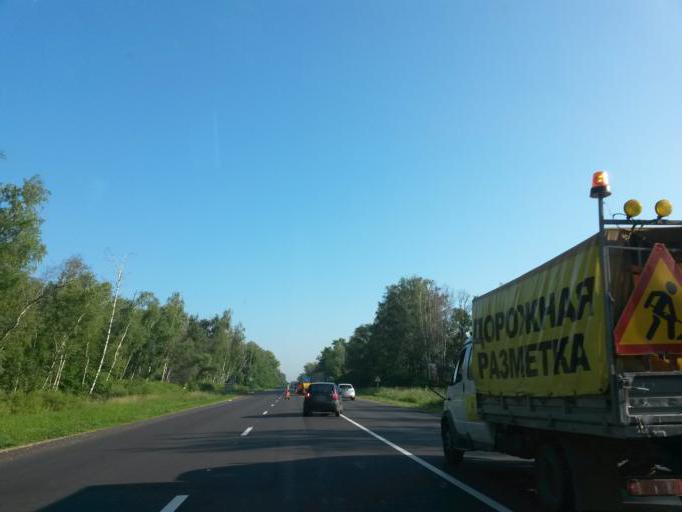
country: RU
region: Moskovskaya
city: Belyye Stolby
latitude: 55.2926
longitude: 37.8193
